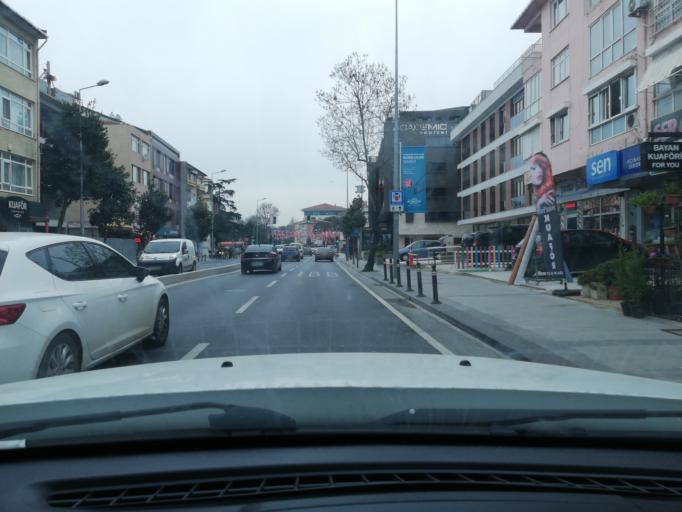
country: TR
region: Istanbul
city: UEskuedar
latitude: 41.0194
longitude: 29.0336
